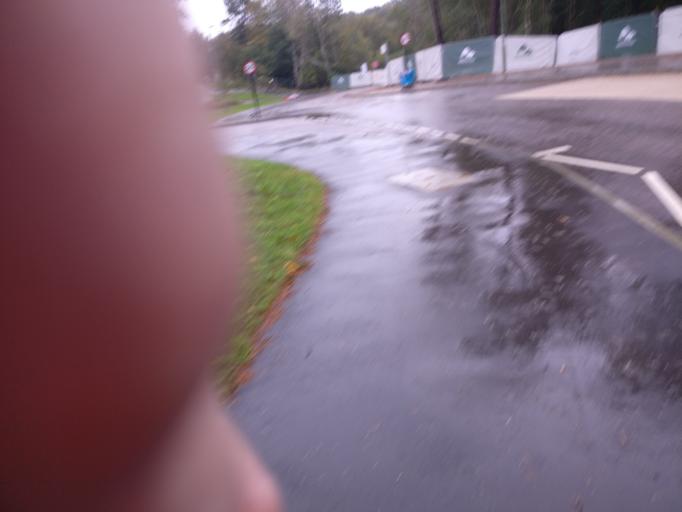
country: GB
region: England
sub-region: Surrey
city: Frimley
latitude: 51.3100
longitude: -0.7016
